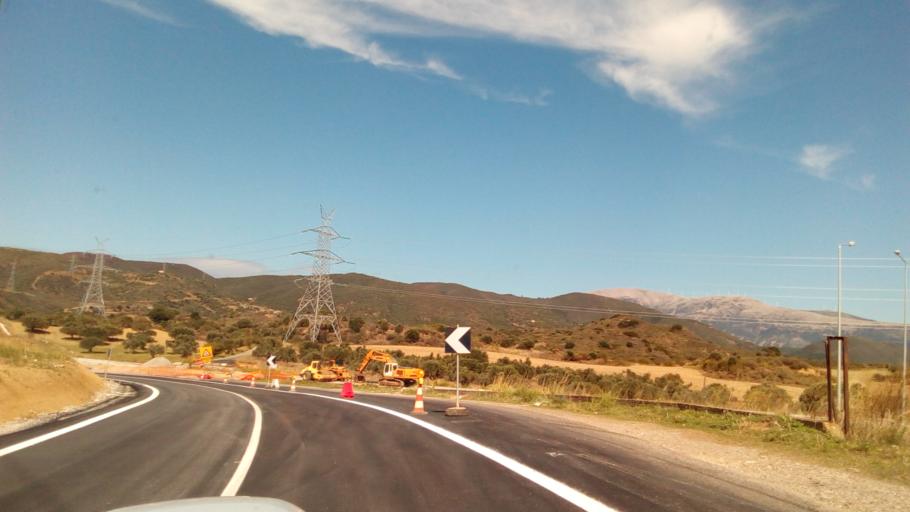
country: GR
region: West Greece
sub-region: Nomos Aitolias kai Akarnanias
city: Antirrio
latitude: 38.3445
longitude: 21.7554
